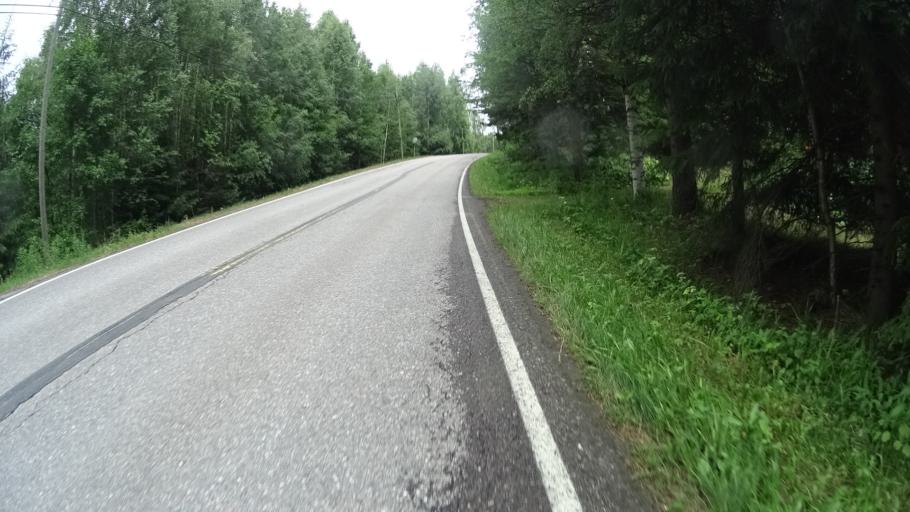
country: FI
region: Uusimaa
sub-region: Helsinki
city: Karkkila
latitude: 60.5765
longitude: 24.3262
